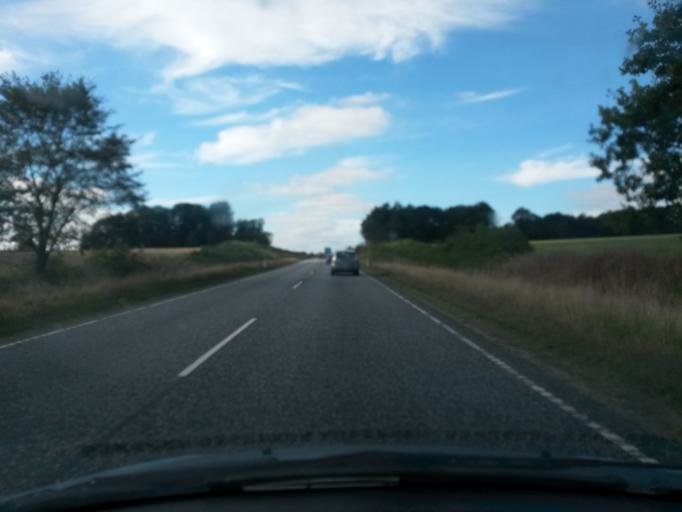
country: DK
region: Central Jutland
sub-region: Herning Kommune
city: Avlum
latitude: 56.2219
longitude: 8.8407
